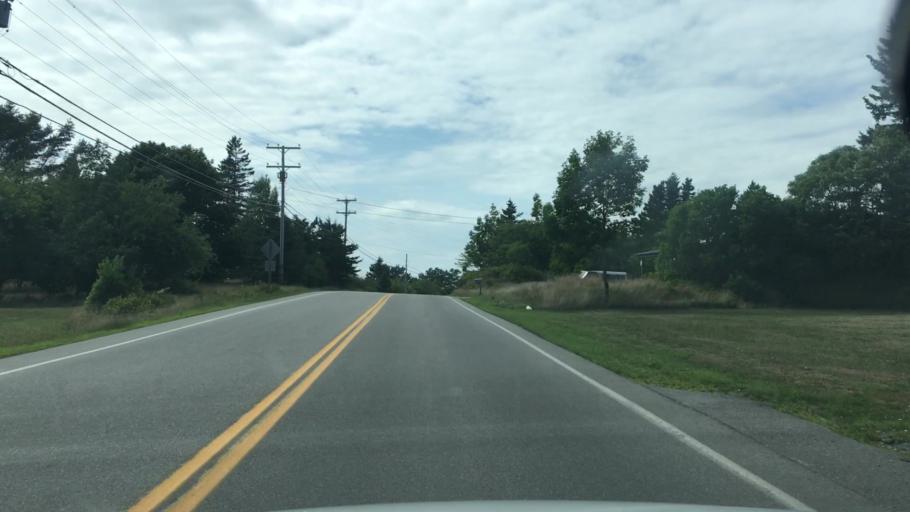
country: US
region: Maine
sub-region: Washington County
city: Eastport
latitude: 44.9127
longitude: -67.0016
